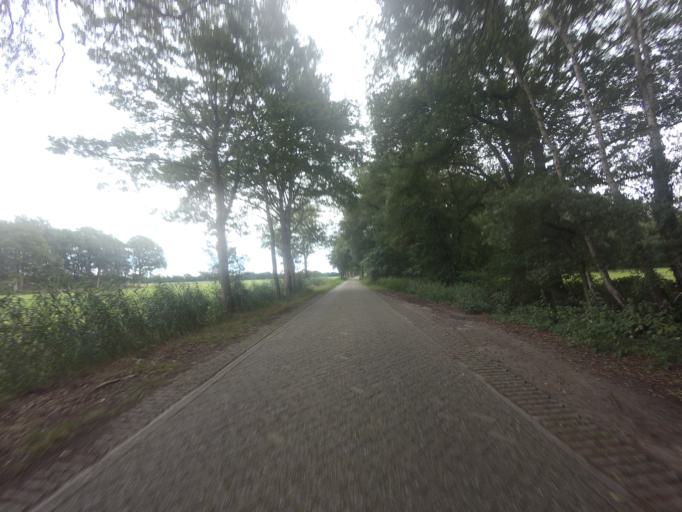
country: NL
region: Overijssel
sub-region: Gemeente Raalte
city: Raalte
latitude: 52.3630
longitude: 6.3029
